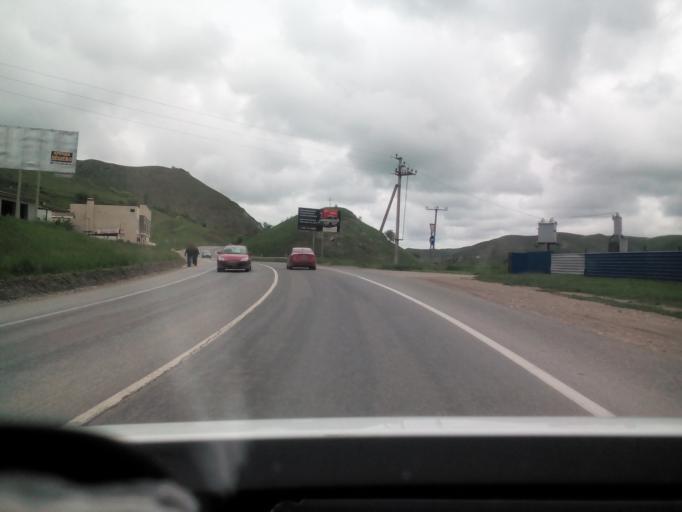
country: RU
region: Stavropol'skiy
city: Yasnaya Polyana
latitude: 43.9735
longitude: 42.7857
